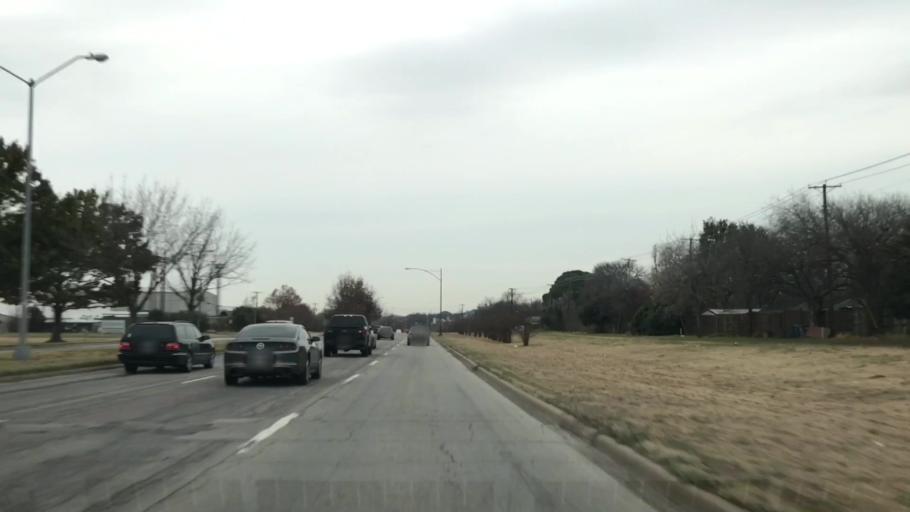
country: US
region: Texas
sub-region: Dallas County
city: University Park
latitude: 32.8541
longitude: -96.8450
